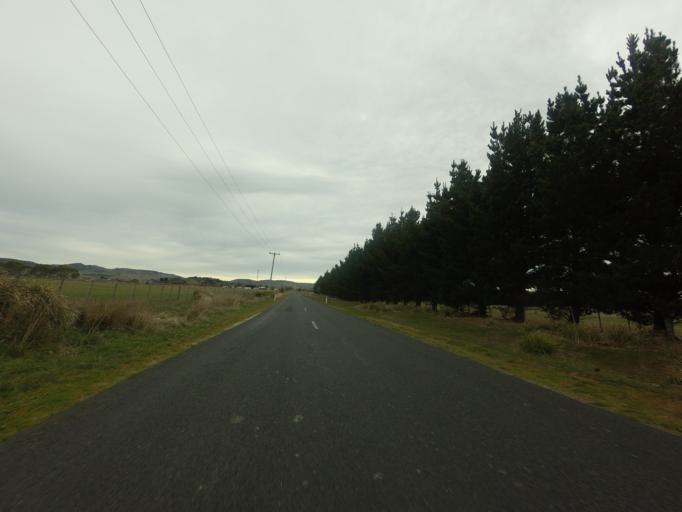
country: AU
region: Tasmania
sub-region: Derwent Valley
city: New Norfolk
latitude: -42.3961
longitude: 147.0051
